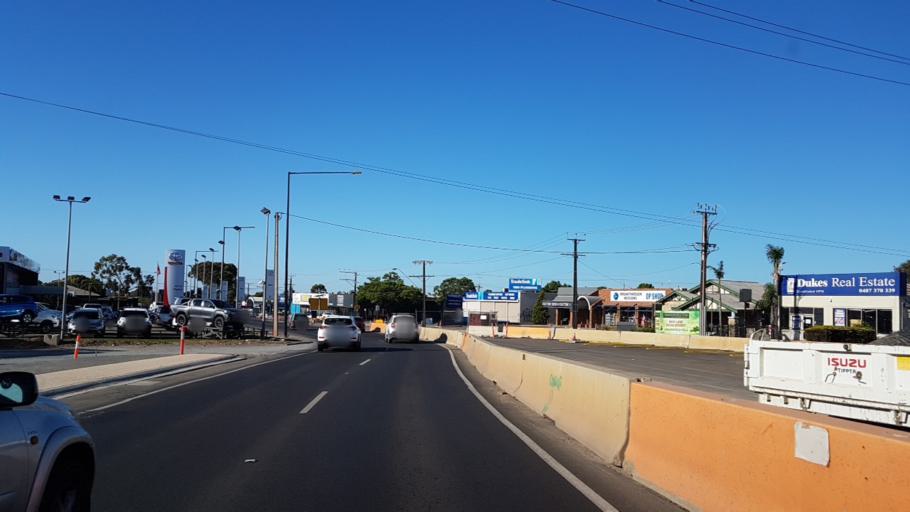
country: AU
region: South Australia
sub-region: Marion
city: Clovelly Park
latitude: -35.0064
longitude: 138.5755
